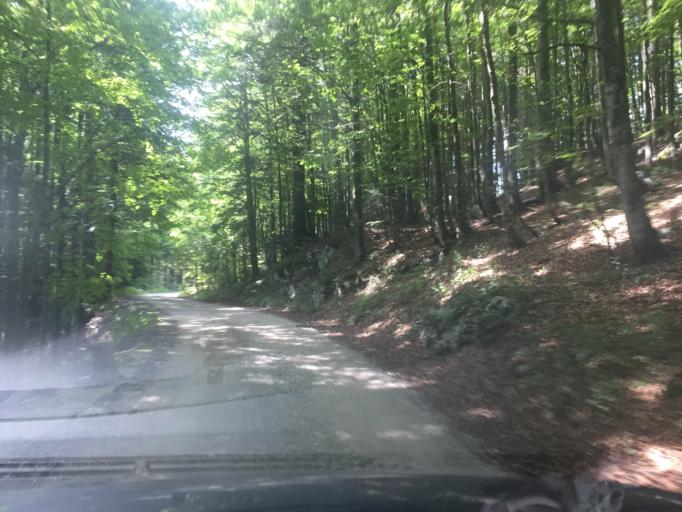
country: SI
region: Ajdovscina
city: Lokavec
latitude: 45.9860
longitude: 13.8387
